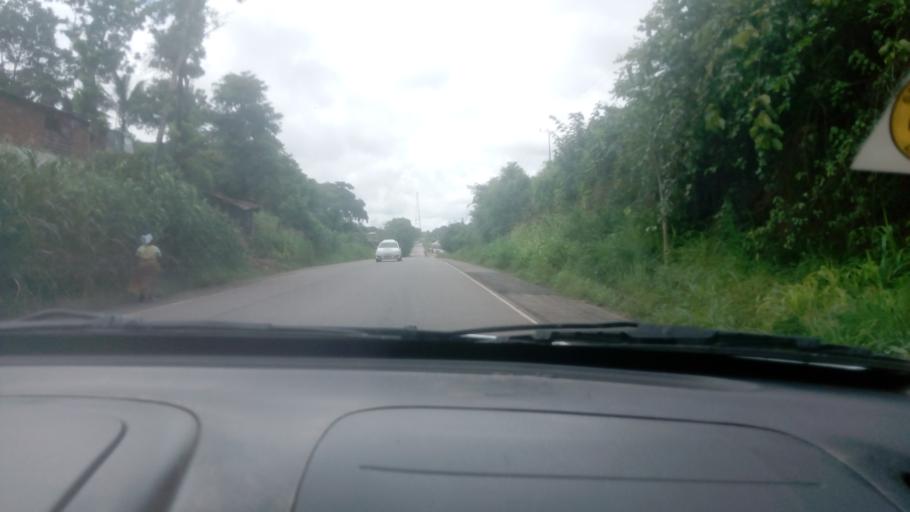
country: SL
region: Northern Province
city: Magburaka
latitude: 8.7289
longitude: -11.9433
